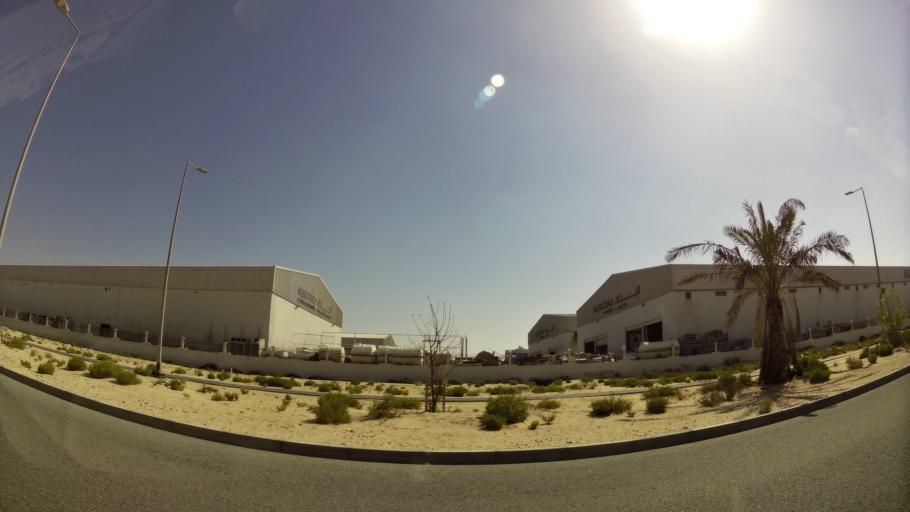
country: AE
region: Dubai
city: Dubai
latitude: 24.9279
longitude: 55.0582
